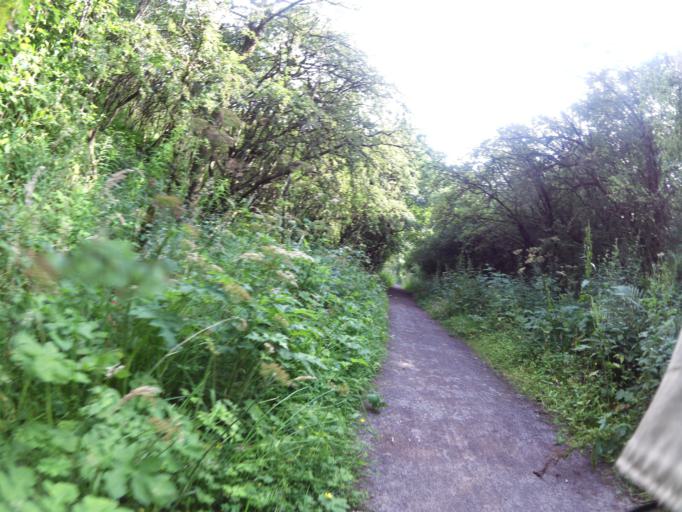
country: GB
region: Scotland
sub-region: Edinburgh
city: Kirkliston
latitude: 55.9690
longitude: -3.3749
